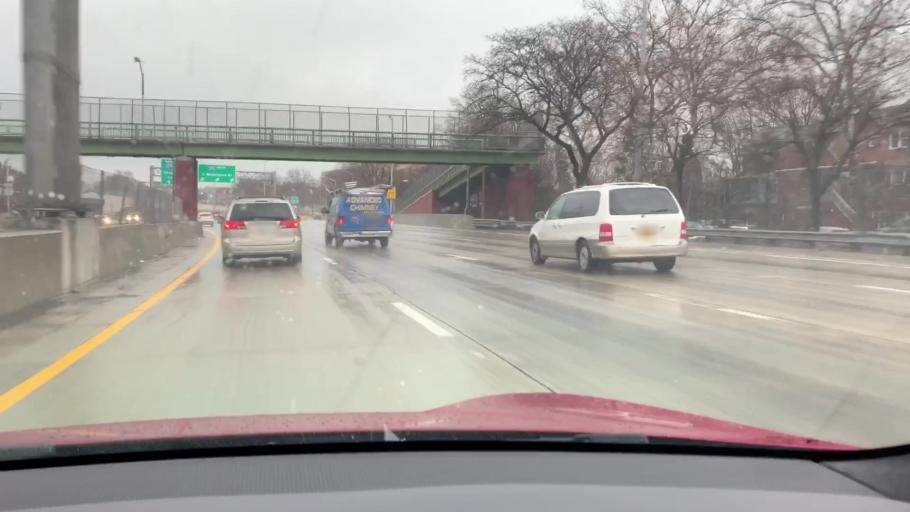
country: US
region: New York
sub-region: Bronx
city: The Bronx
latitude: 40.8384
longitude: -73.8246
